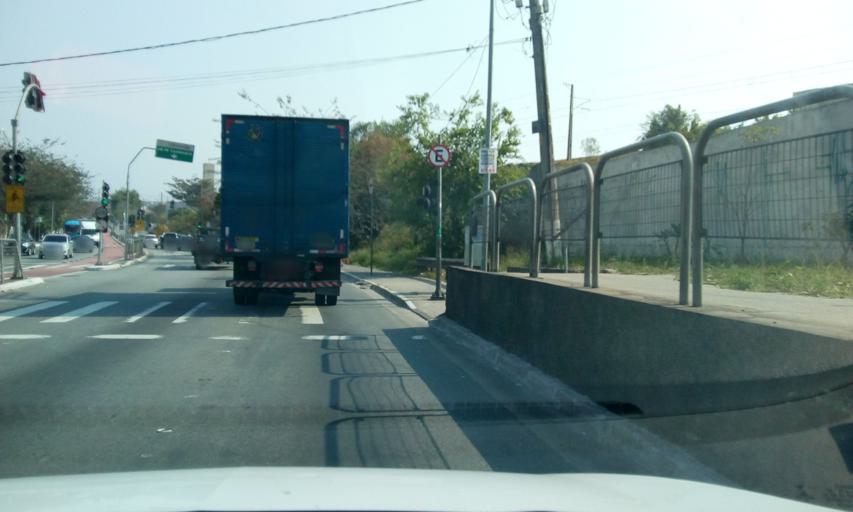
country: BR
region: Sao Paulo
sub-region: Diadema
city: Diadema
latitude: -23.7043
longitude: -46.6870
